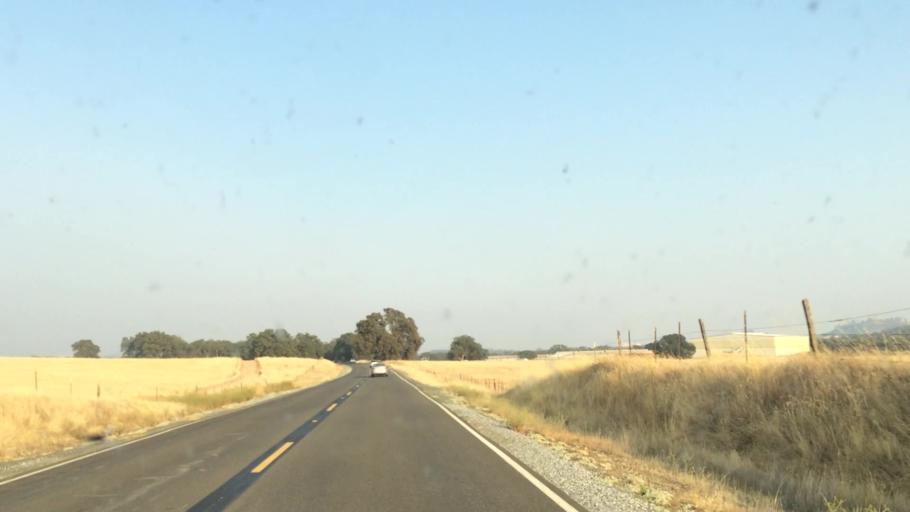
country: US
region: California
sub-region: Amador County
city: Ione
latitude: 38.4007
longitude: -121.0144
